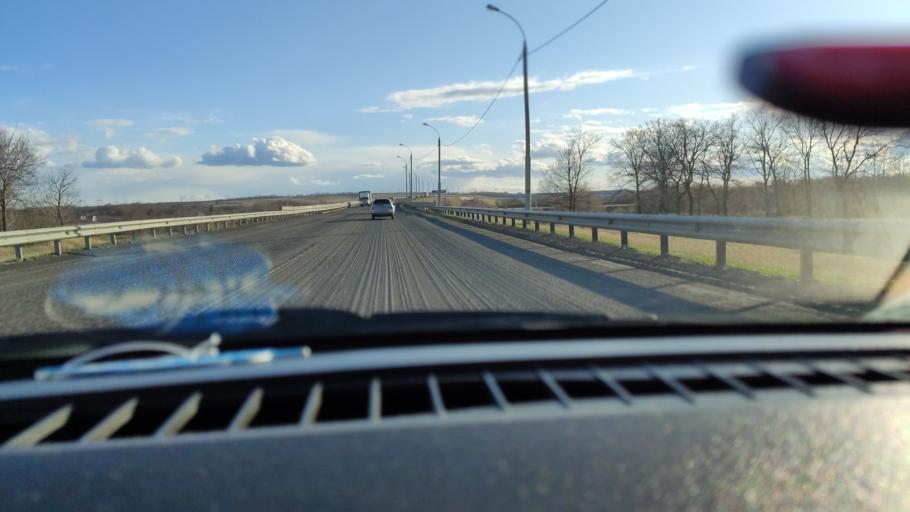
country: RU
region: Saratov
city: Yelshanka
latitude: 51.8021
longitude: 46.1895
